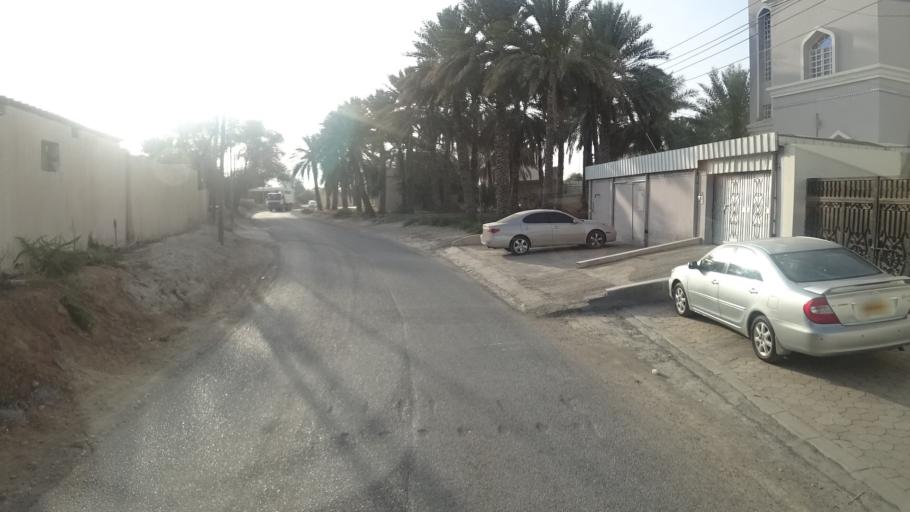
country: OM
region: Muhafazat ad Dakhiliyah
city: Bahla'
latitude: 23.0984
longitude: 57.3049
